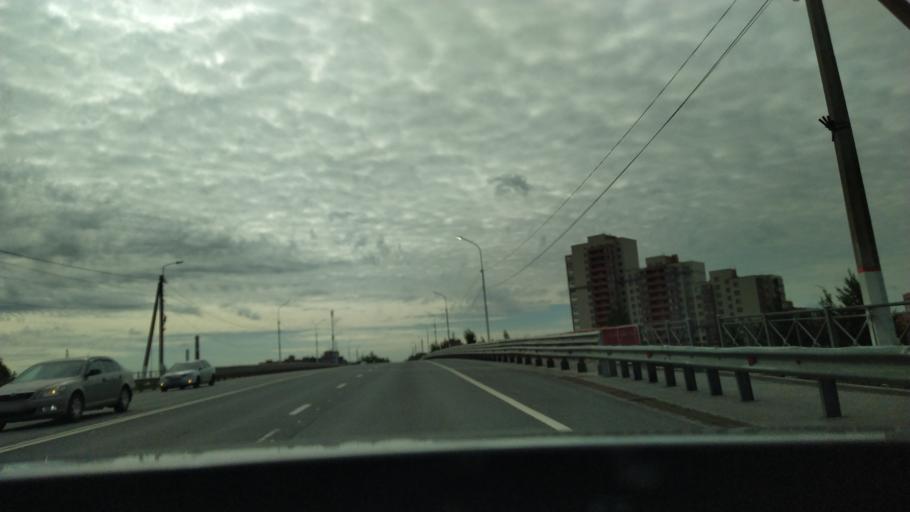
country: RU
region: Leningrad
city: Tosno
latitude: 59.5520
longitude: 30.8569
